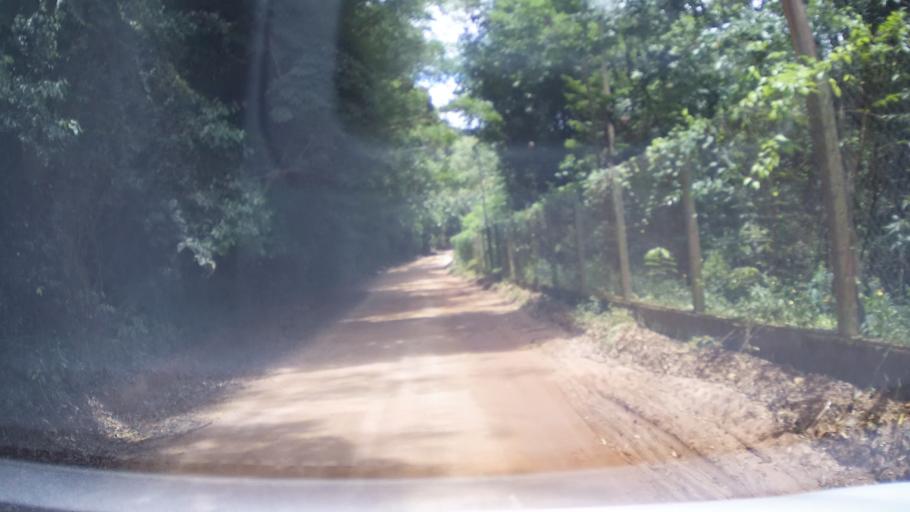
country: BR
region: Sao Paulo
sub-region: Vinhedo
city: Vinhedo
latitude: -22.9950
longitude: -46.9655
